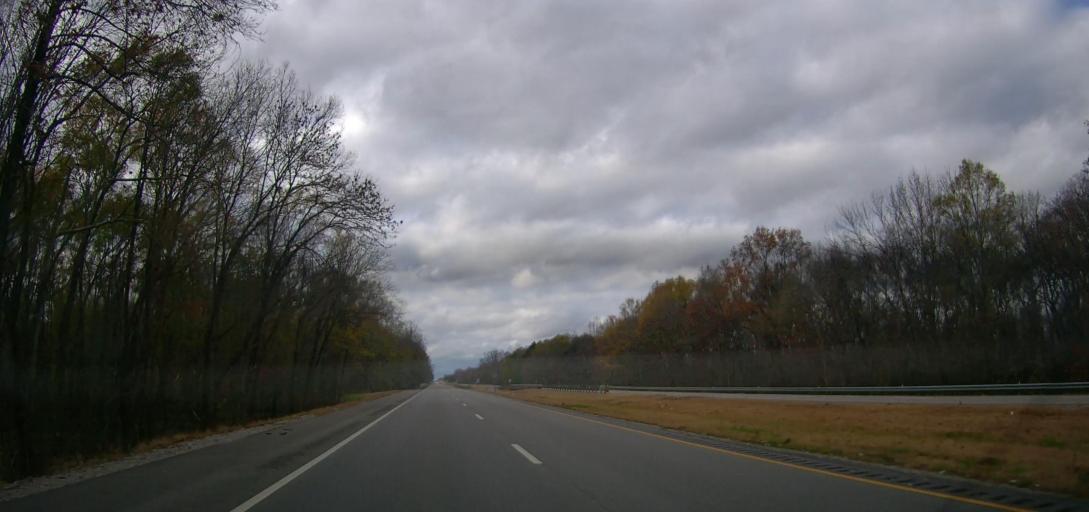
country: US
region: Alabama
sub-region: Lawrence County
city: Town Creek
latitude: 34.6321
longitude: -87.4875
